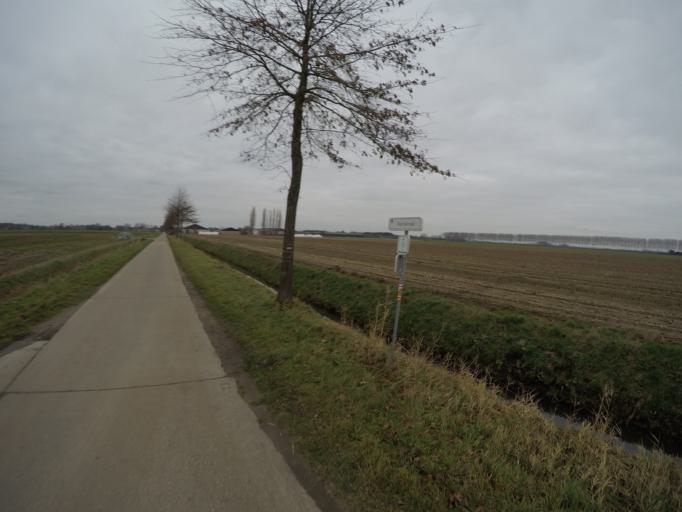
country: BE
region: Flanders
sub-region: Provincie Oost-Vlaanderen
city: Sint-Gillis-Waas
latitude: 51.2507
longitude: 4.1048
